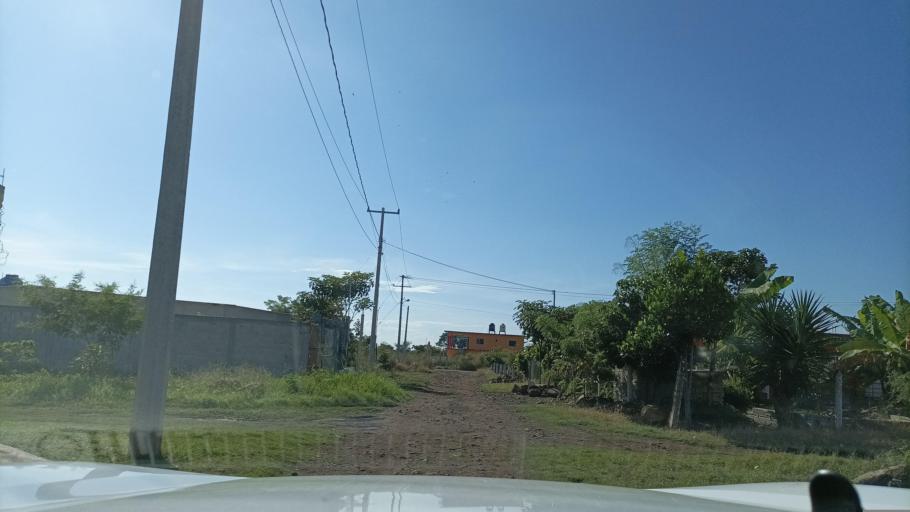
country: MX
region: Veracruz
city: Paso del Macho
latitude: 18.9730
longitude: -96.7132
